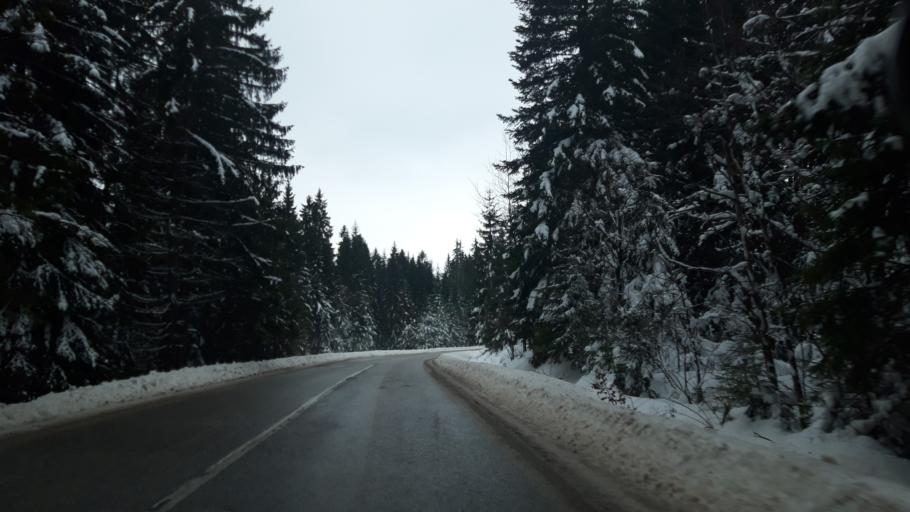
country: BA
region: Republika Srpska
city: Han Pijesak
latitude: 44.0535
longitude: 18.9355
